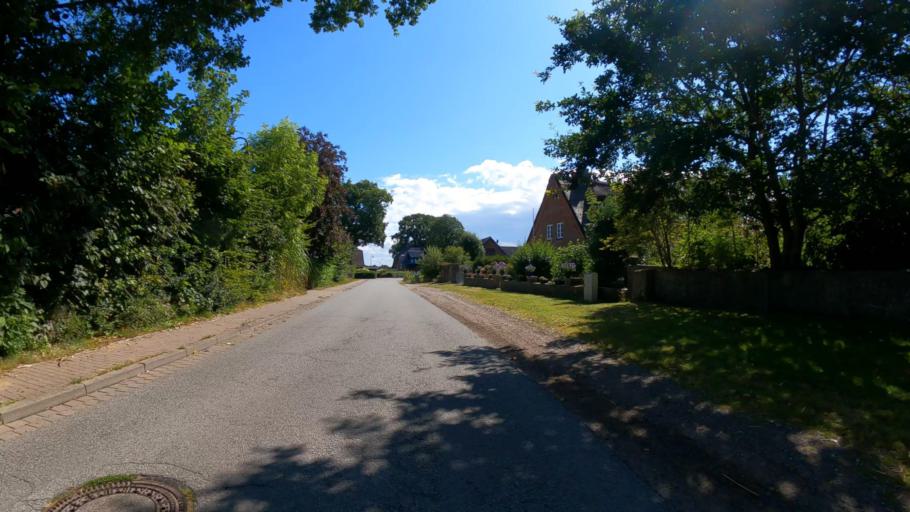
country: DE
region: Schleswig-Holstein
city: Armstedt
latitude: 53.9700
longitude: 9.8527
